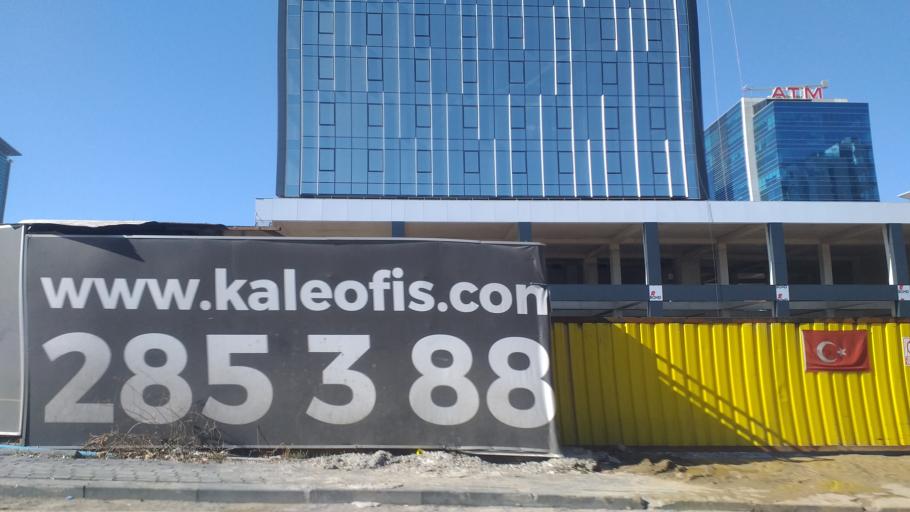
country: TR
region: Ankara
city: Ankara
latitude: 39.8984
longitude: 32.8135
